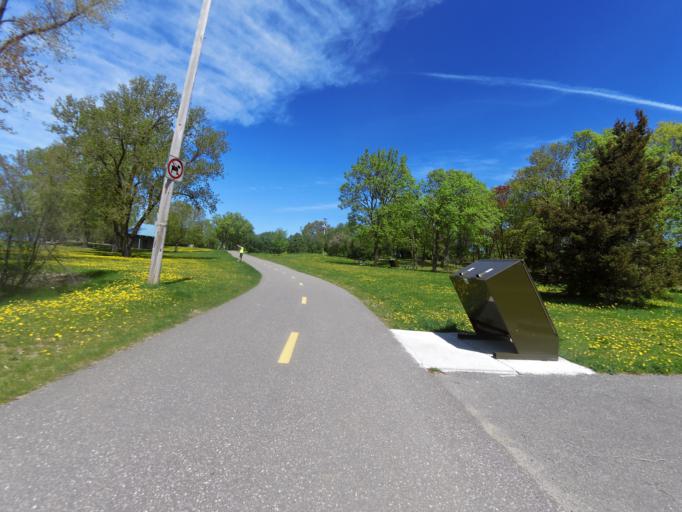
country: CA
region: Ontario
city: Bells Corners
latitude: 45.3974
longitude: -75.8591
